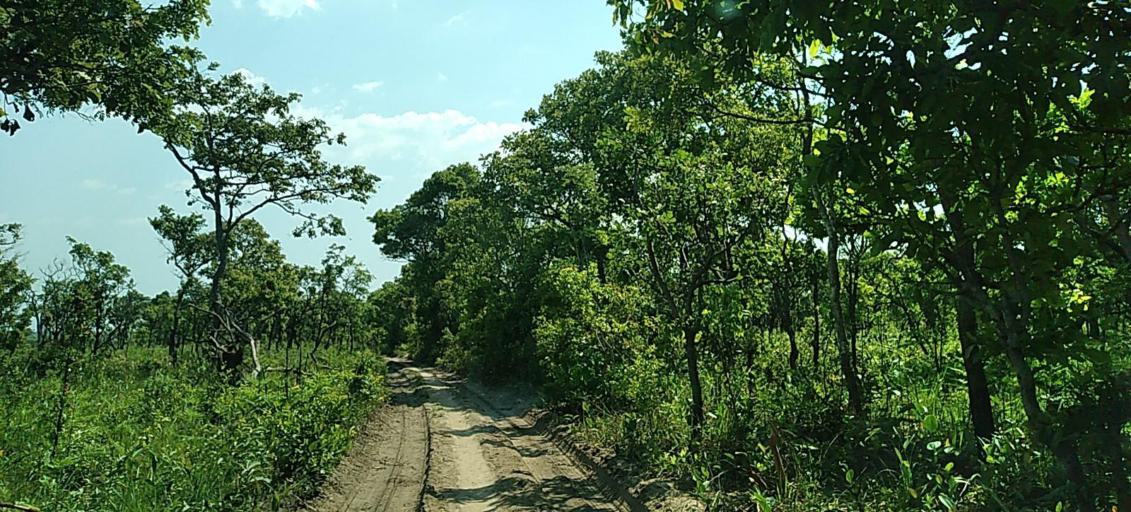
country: CD
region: Katanga
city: Kolwezi
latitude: -11.2589
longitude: 25.0107
